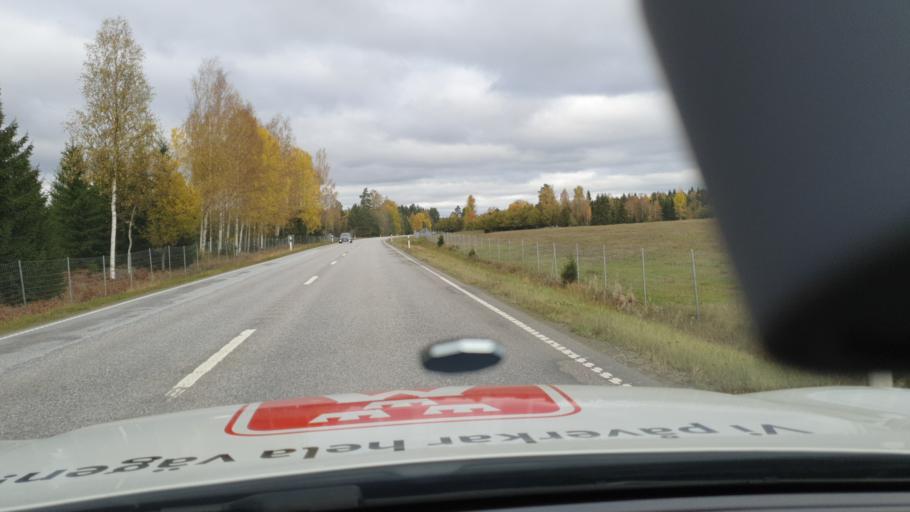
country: SE
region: OErebro
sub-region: Hallsbergs Kommun
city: Palsboda
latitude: 58.9827
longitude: 15.4093
